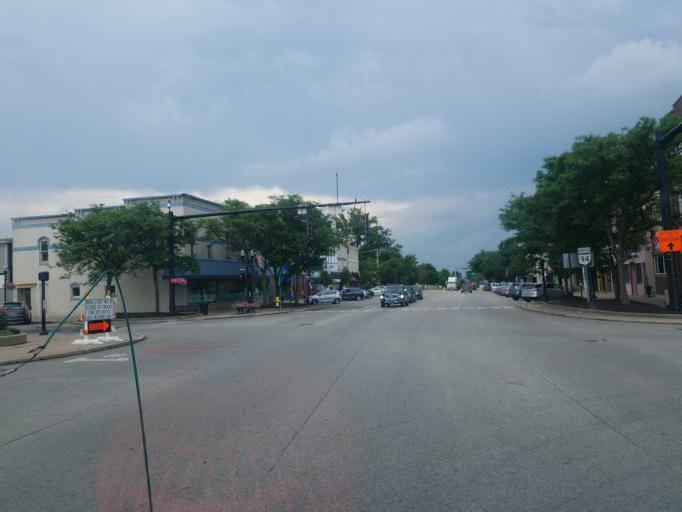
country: US
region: Ohio
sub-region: Medina County
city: Wadsworth
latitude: 41.0256
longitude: -81.7297
